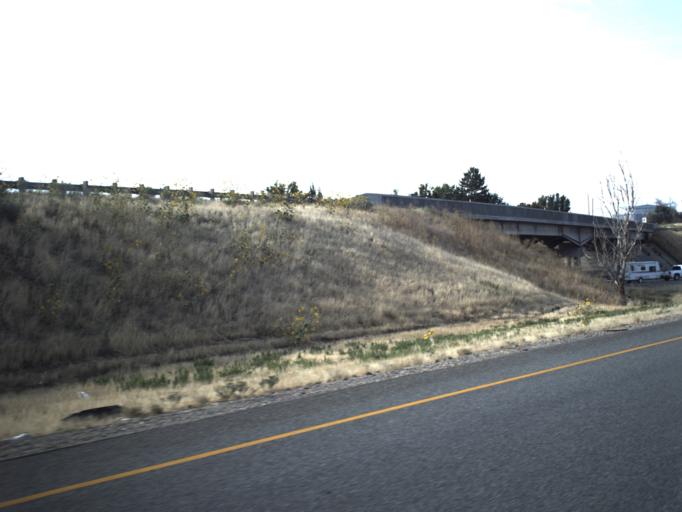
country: US
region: Utah
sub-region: Weber County
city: Riverdale
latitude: 41.1841
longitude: -112.0107
